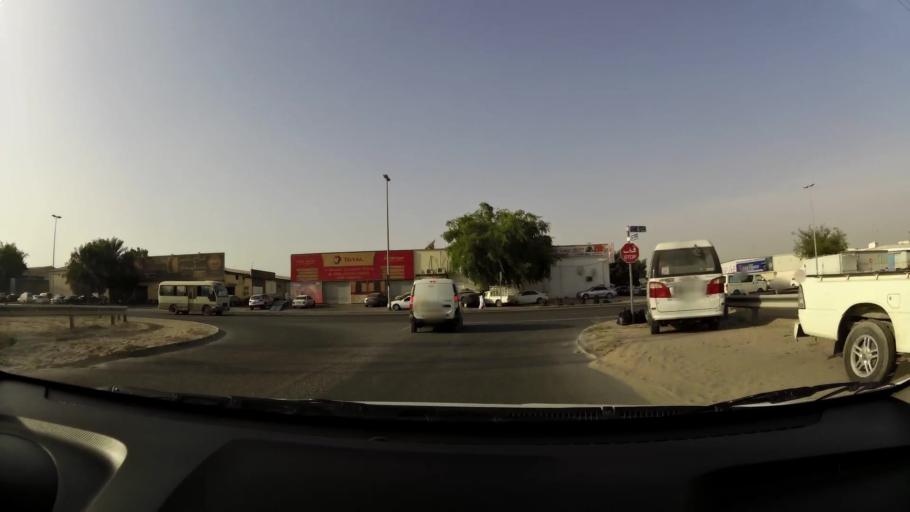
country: AE
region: Ash Shariqah
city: Sharjah
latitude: 25.2231
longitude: 55.3733
